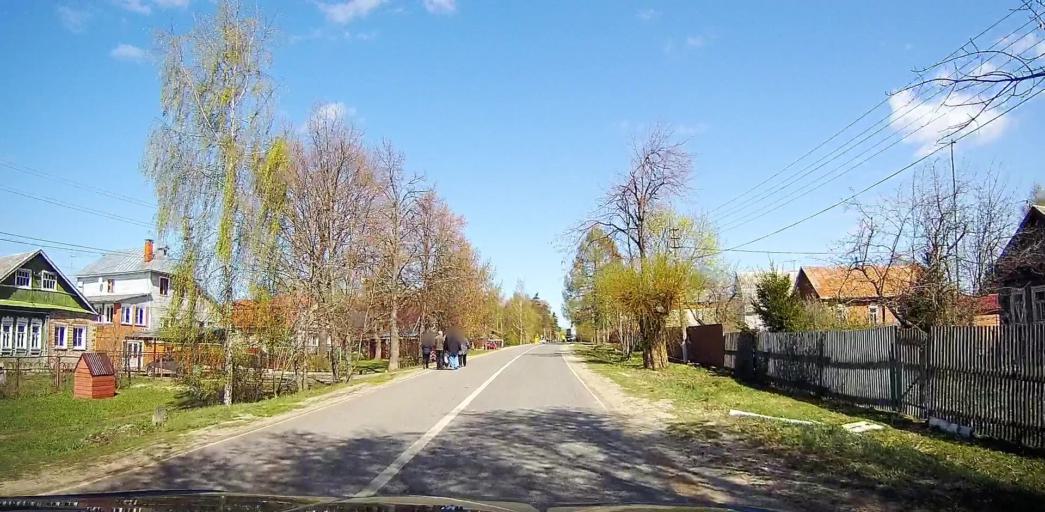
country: RU
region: Moskovskaya
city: Ramenskoye
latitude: 55.6244
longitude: 38.3023
